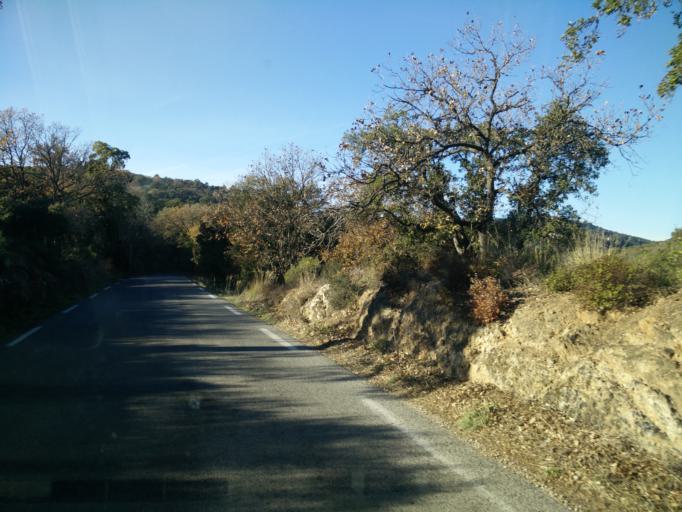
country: FR
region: Provence-Alpes-Cote d'Azur
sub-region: Departement du Var
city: Le Plan-de-la-Tour
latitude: 43.2908
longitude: 6.5690
